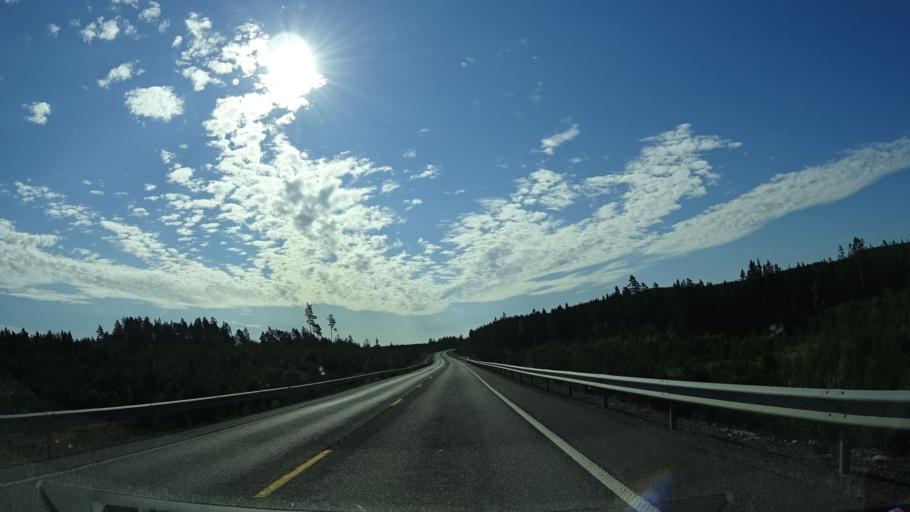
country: NO
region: Ostfold
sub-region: Marker
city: Orje
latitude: 59.5371
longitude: 11.5532
